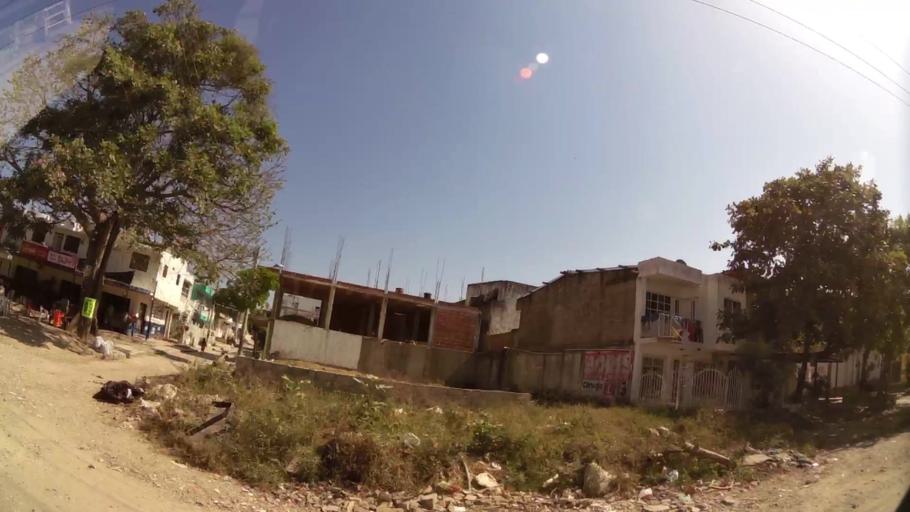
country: CO
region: Bolivar
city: Cartagena
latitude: 10.3750
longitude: -75.4970
